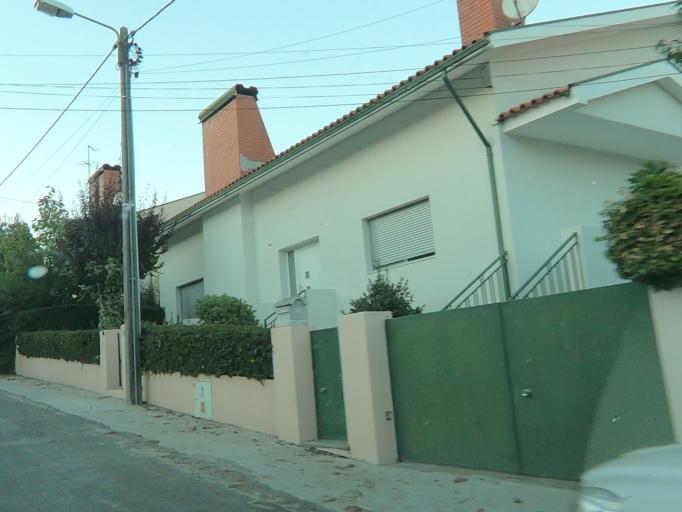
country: PT
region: Vila Real
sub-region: Vila Real
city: Vila Real
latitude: 41.3055
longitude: -7.7643
